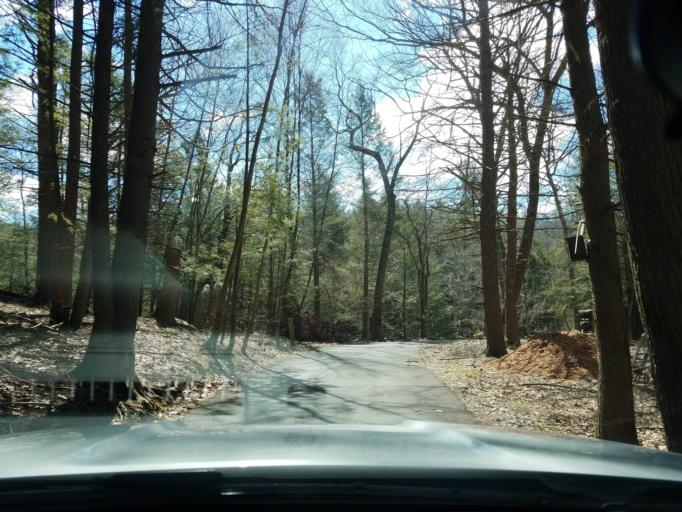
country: US
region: Connecticut
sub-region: Tolland County
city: Coventry Lake
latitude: 41.7670
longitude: -72.3924
